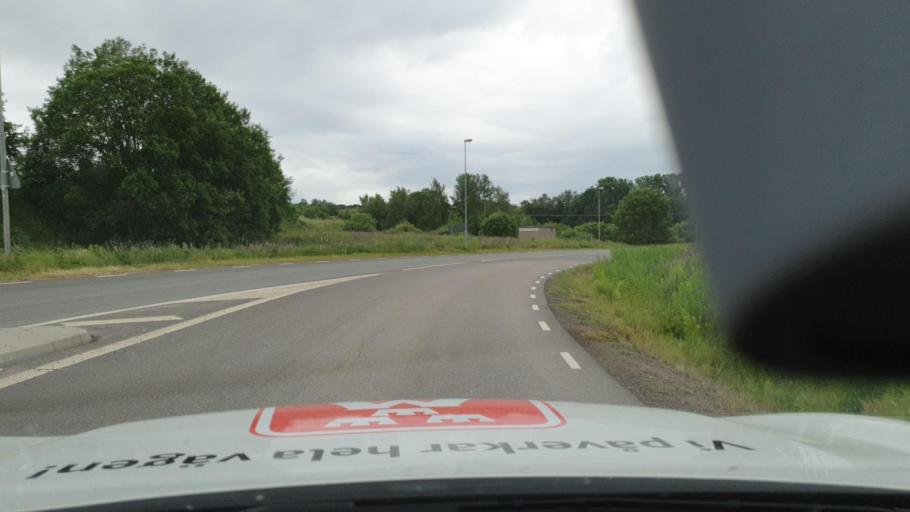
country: SE
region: Vaestra Goetaland
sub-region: Skovde Kommun
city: Skoevde
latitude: 58.3829
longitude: 13.8825
